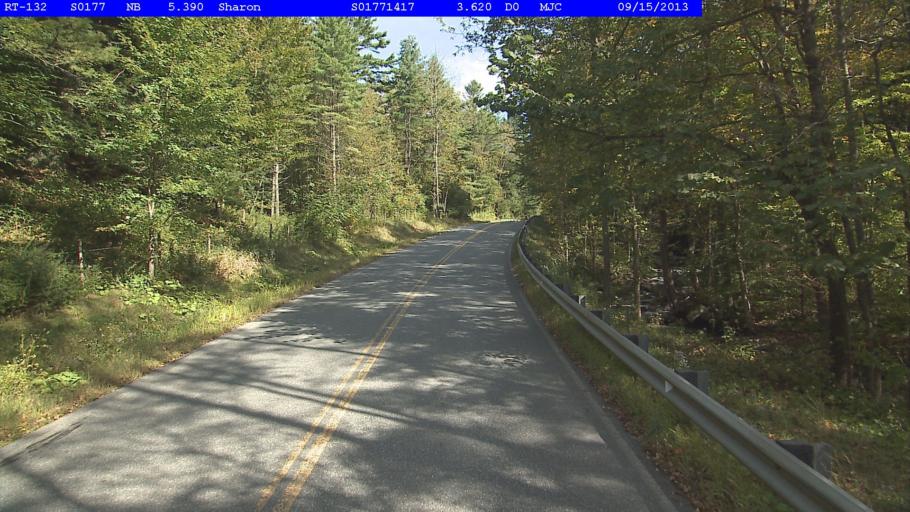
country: US
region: Vermont
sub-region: Windsor County
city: Woodstock
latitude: 43.7908
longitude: -72.4486
